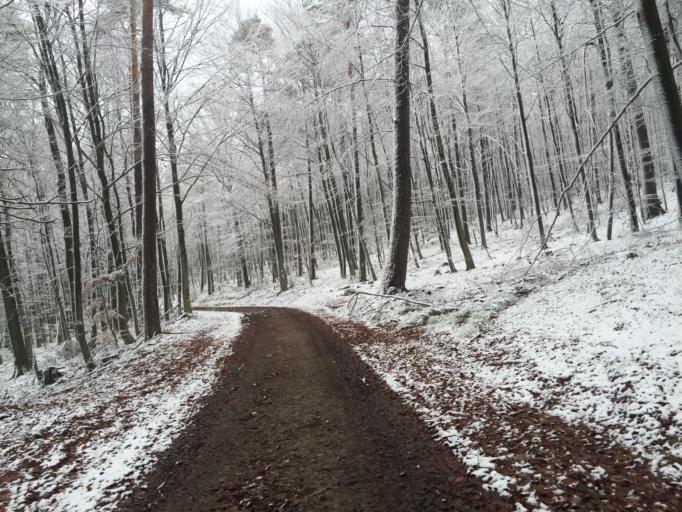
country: DE
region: Hesse
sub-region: Regierungsbezirk Darmstadt
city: Wald-Michelbach
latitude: 49.5648
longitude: 8.8801
